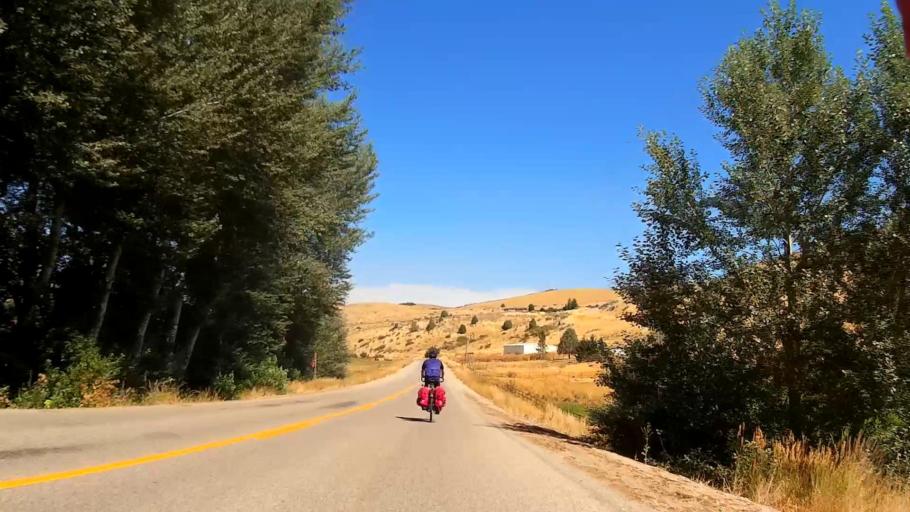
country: US
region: Idaho
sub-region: Bannock County
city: Pocatello
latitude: 42.7563
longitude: -112.2153
